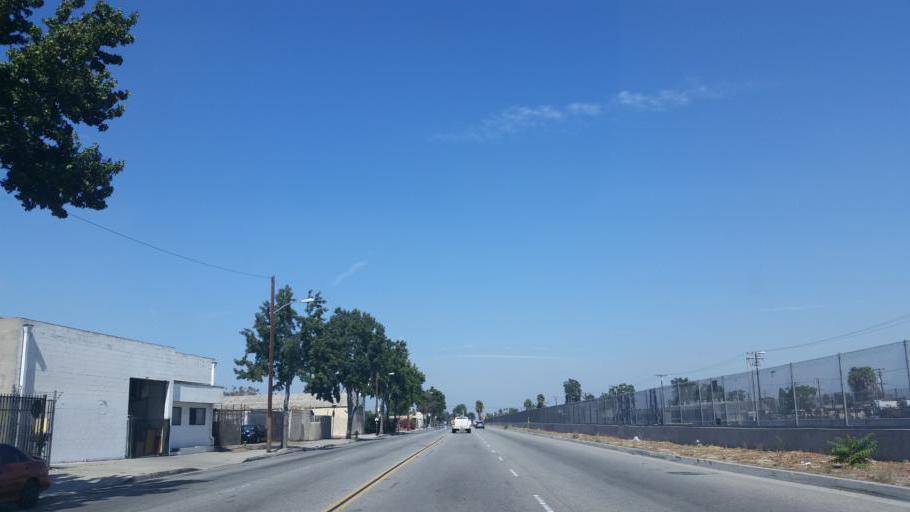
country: US
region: California
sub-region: Los Angeles County
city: Compton
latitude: 33.8847
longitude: -118.2186
